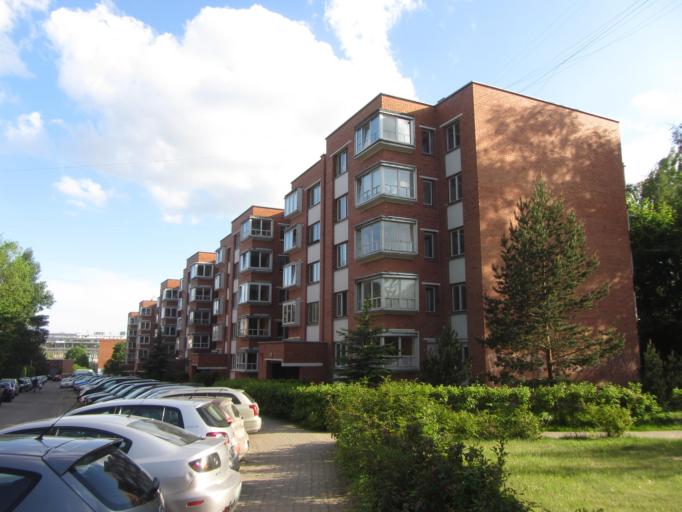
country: LT
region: Vilnius County
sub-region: Vilnius
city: Fabijoniskes
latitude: 54.7410
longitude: 25.2658
